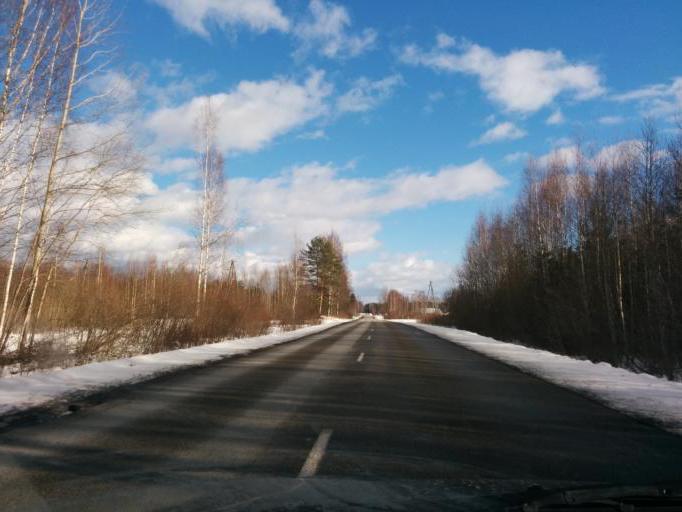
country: LV
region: Gulbenes Rajons
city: Gulbene
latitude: 57.1926
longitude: 26.9727
